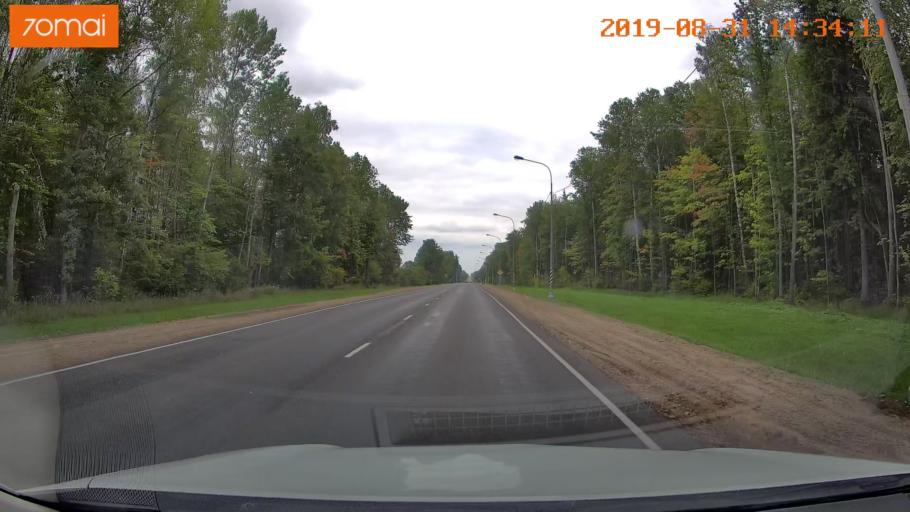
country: RU
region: Smolensk
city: Yekimovichi
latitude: 54.1561
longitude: 33.4331
